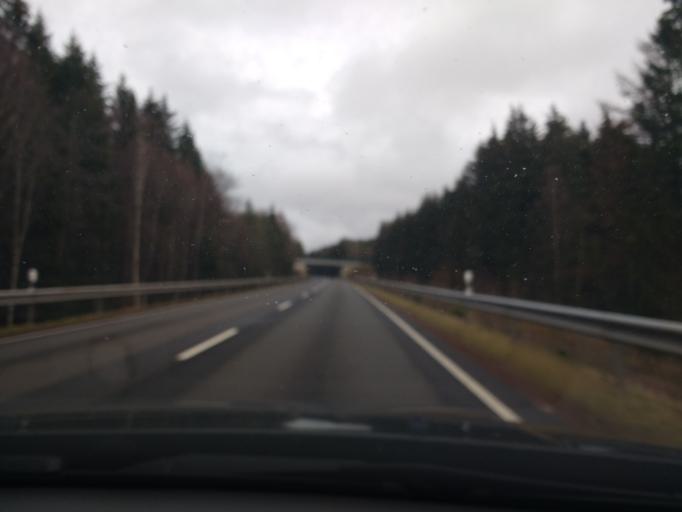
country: DE
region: Rheinland-Pfalz
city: Hermeskeil
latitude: 49.6784
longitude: 6.9353
